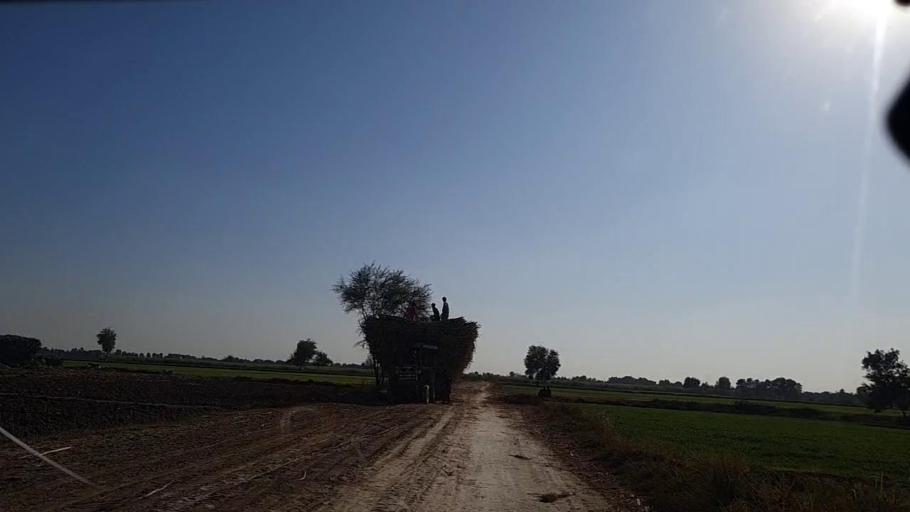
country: PK
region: Sindh
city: Khanpur
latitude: 27.7765
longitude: 69.3659
